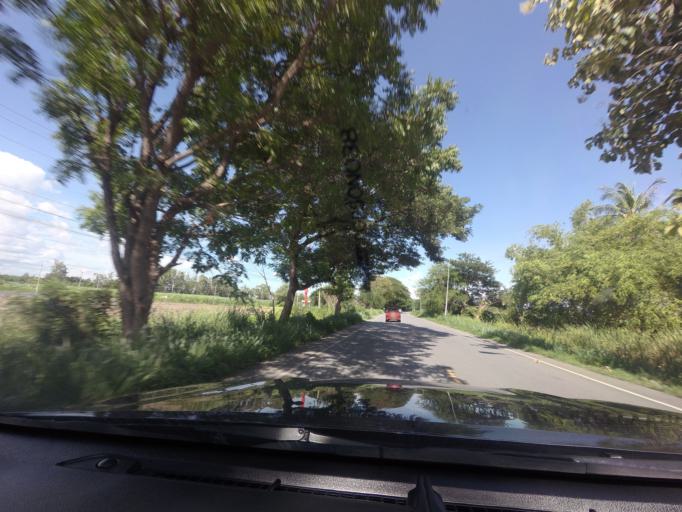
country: TH
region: Kanchanaburi
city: Phanom Thuan
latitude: 14.1730
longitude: 99.8486
